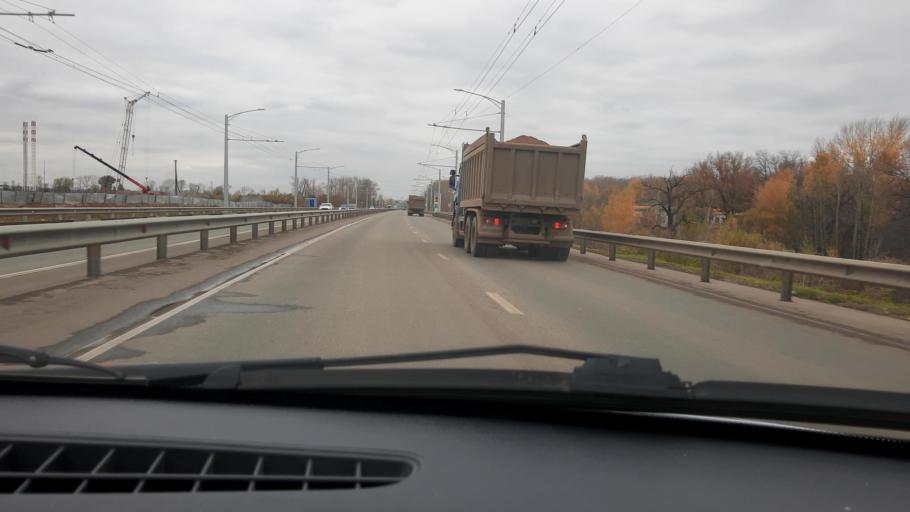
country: RU
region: Bashkortostan
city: Mikhaylovka
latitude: 54.7715
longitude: 55.9066
